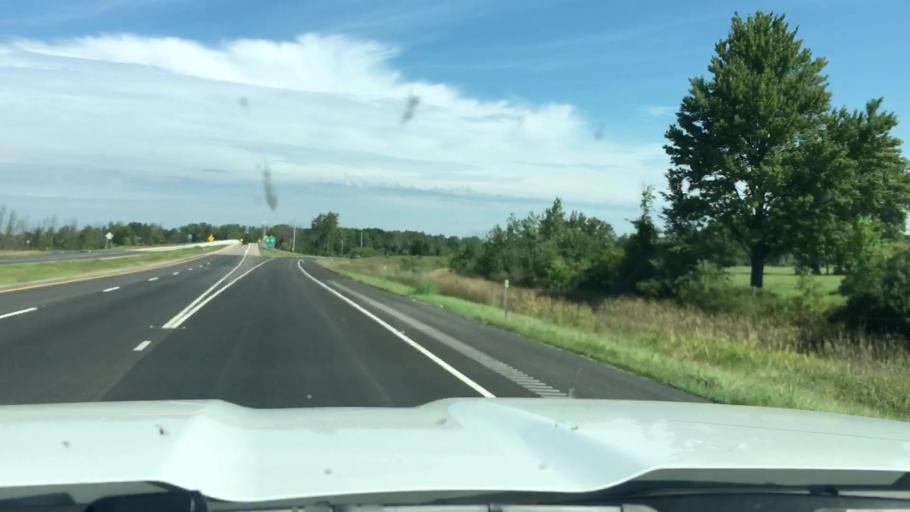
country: US
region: Michigan
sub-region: Saginaw County
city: Freeland
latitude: 43.5932
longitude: -84.1391
